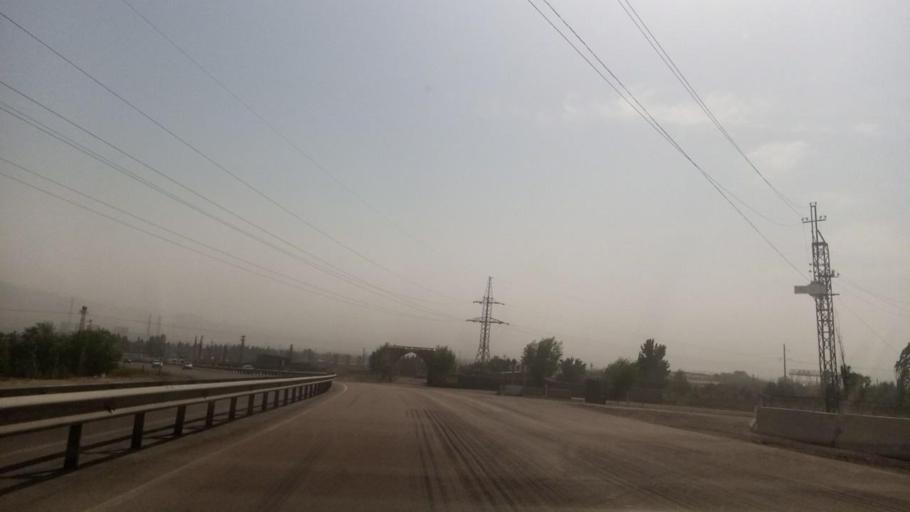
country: UZ
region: Toshkent
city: Angren
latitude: 41.0314
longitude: 70.1386
